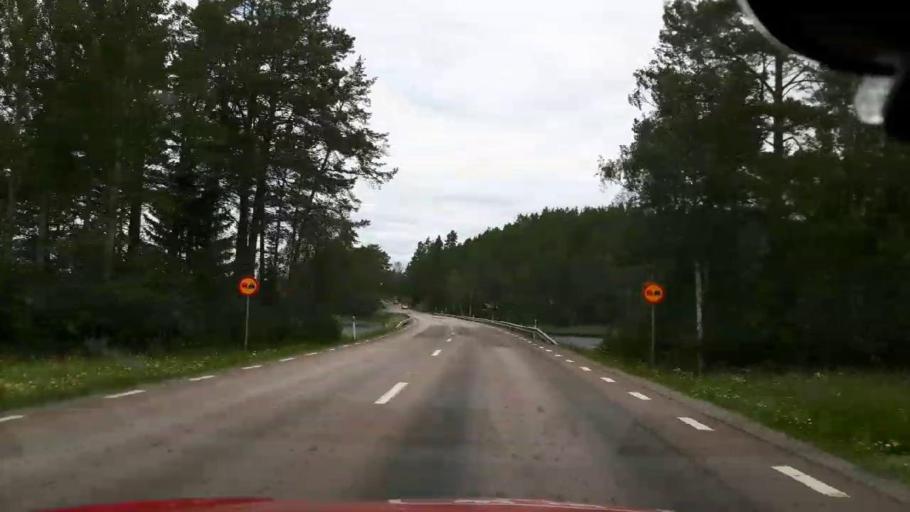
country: SE
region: Jaemtland
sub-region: OEstersunds Kommun
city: Brunflo
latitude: 63.0081
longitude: 14.9574
